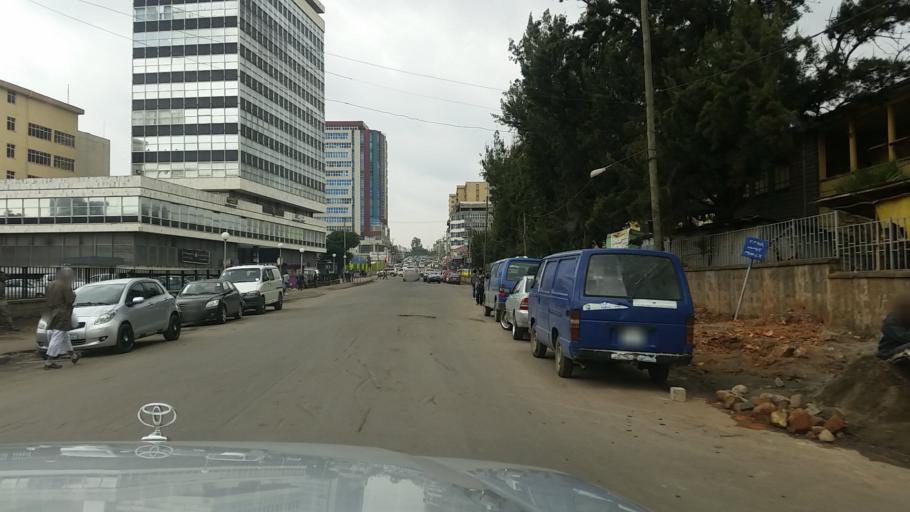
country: ET
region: Adis Abeba
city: Addis Ababa
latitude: 9.0122
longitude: 38.7496
